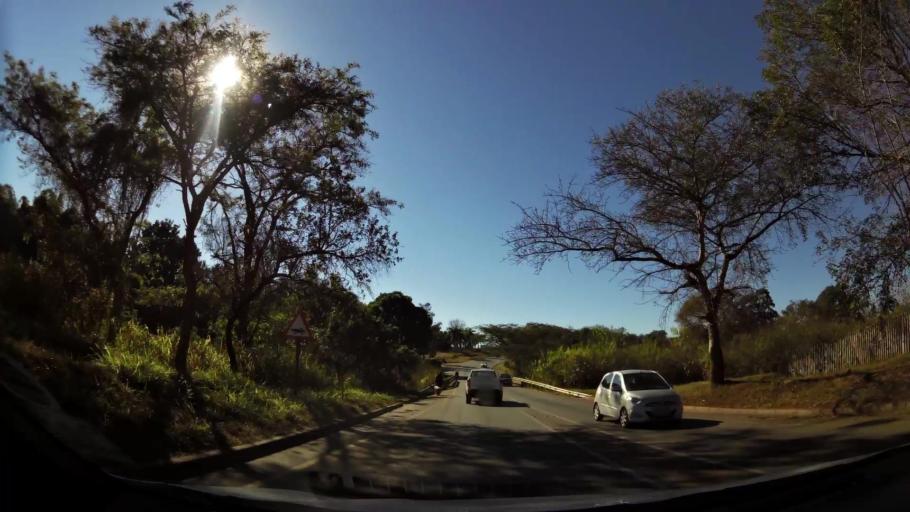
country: ZA
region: Limpopo
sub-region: Mopani District Municipality
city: Tzaneen
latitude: -23.8366
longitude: 30.1777
